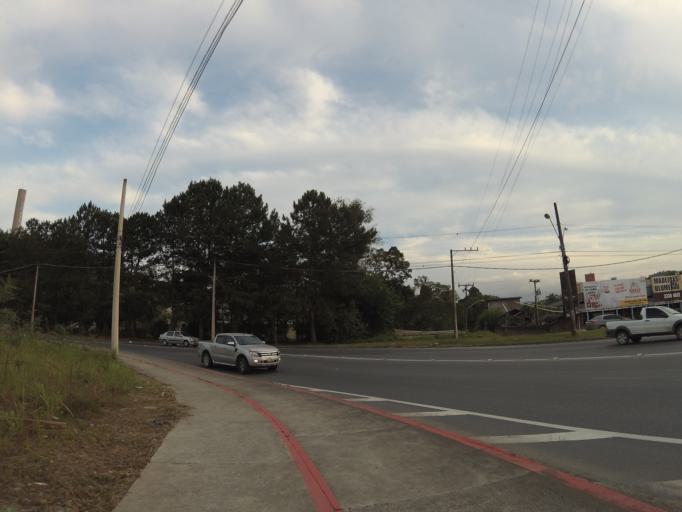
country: BR
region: Santa Catarina
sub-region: Blumenau
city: Blumenau
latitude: -26.8974
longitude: -49.1359
